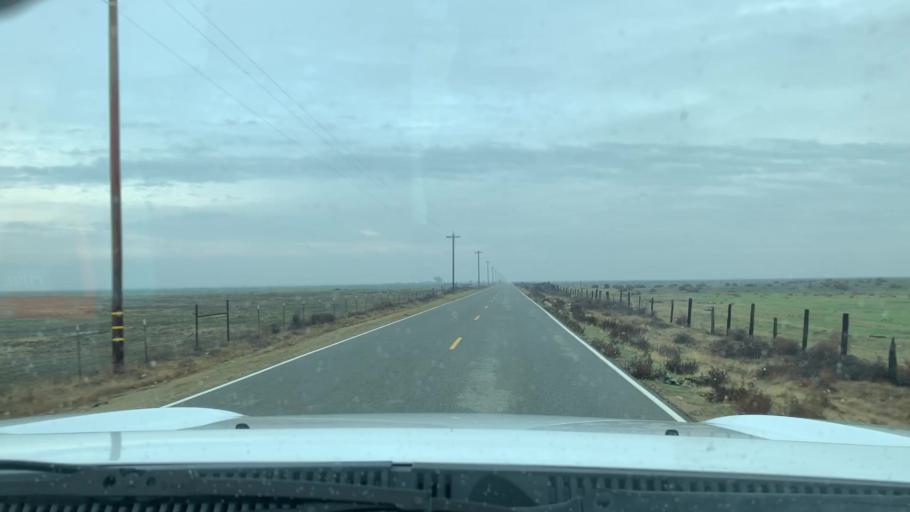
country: US
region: California
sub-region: Kern County
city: Lost Hills
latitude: 35.6871
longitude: -119.5798
